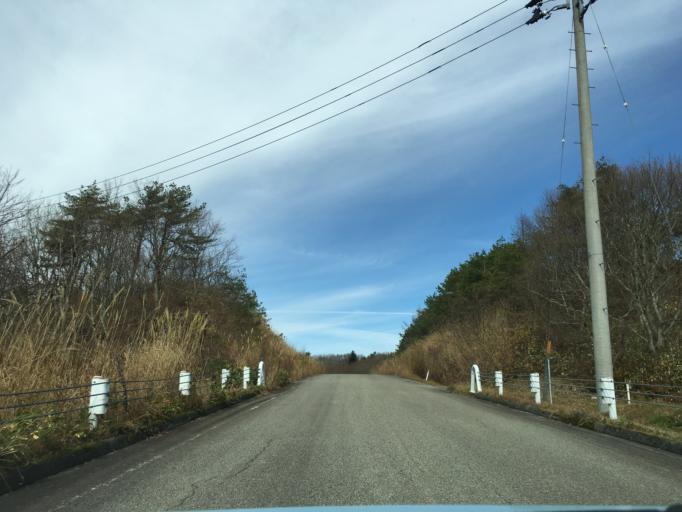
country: JP
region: Fukushima
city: Inawashiro
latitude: 37.4700
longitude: 139.9897
